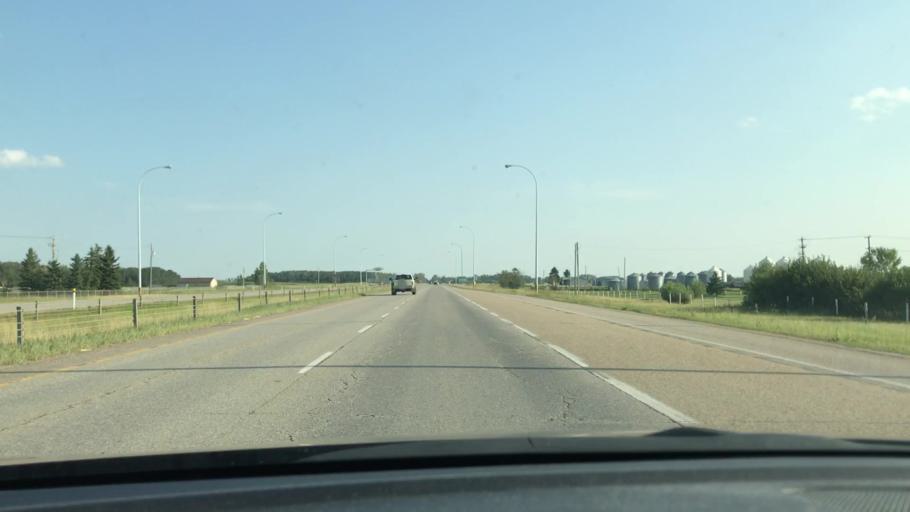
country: CA
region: Alberta
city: Leduc
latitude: 53.2524
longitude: -113.5619
